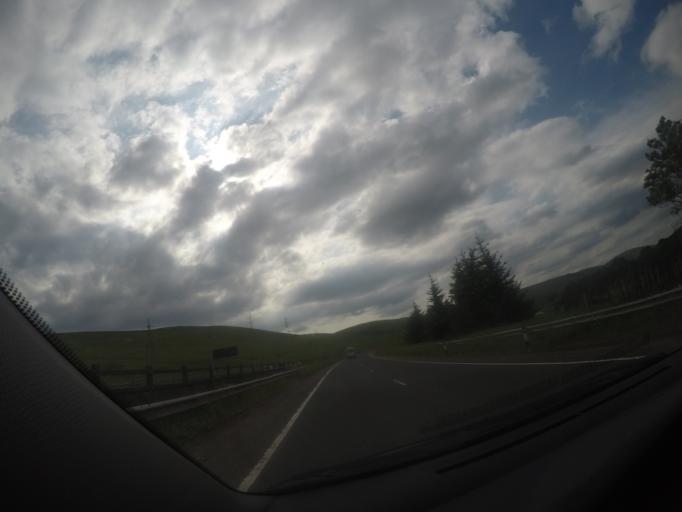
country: GB
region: Scotland
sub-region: South Lanarkshire
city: Douglas
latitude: 55.4671
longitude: -3.6781
